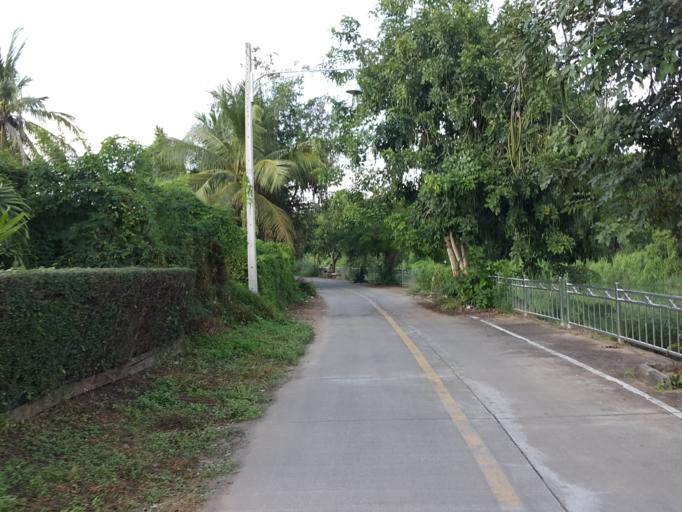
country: TH
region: Lampang
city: Lampang
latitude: 18.2960
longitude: 99.5127
